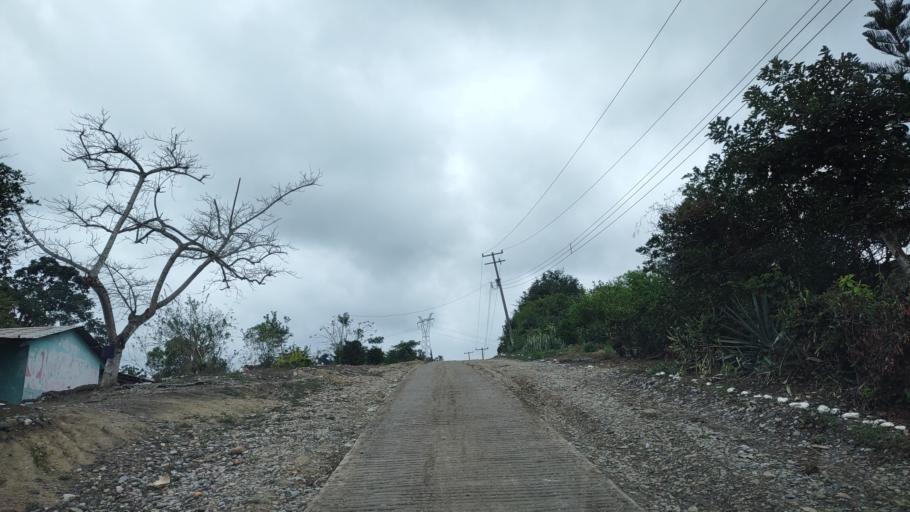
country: MX
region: Veracruz
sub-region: Coatzintla
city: Manuel Maria Contreras
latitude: 20.4063
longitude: -97.4543
